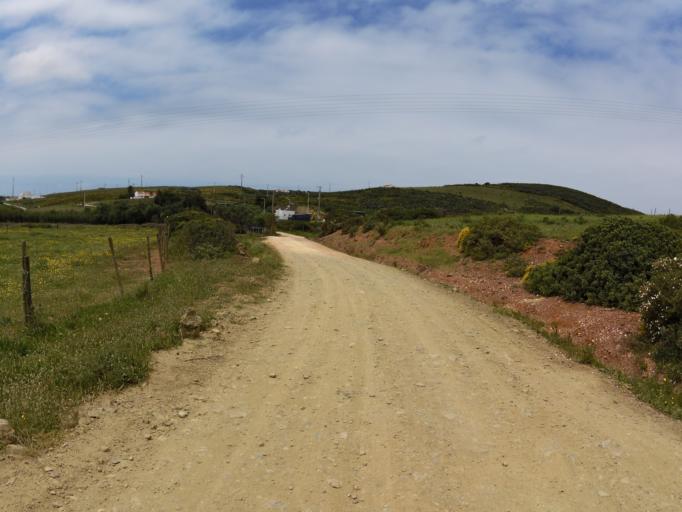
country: PT
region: Faro
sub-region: Vila do Bispo
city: Vila do Bispo
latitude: 37.0881
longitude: -8.9011
